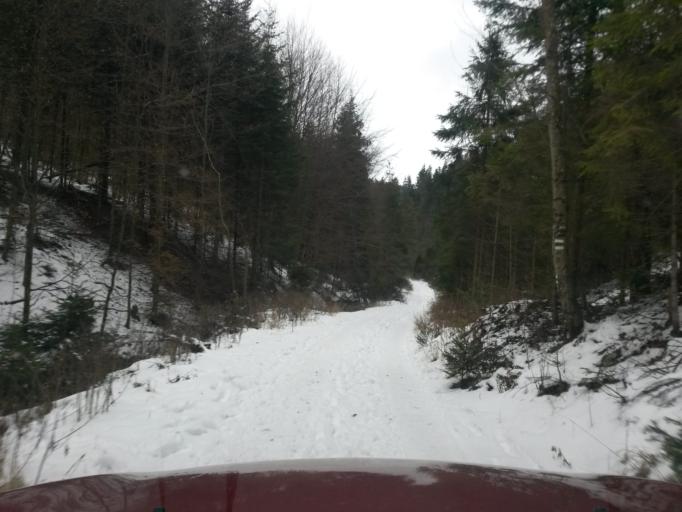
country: SK
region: Kosicky
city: Spisska Nova Ves
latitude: 48.8765
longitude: 20.5836
